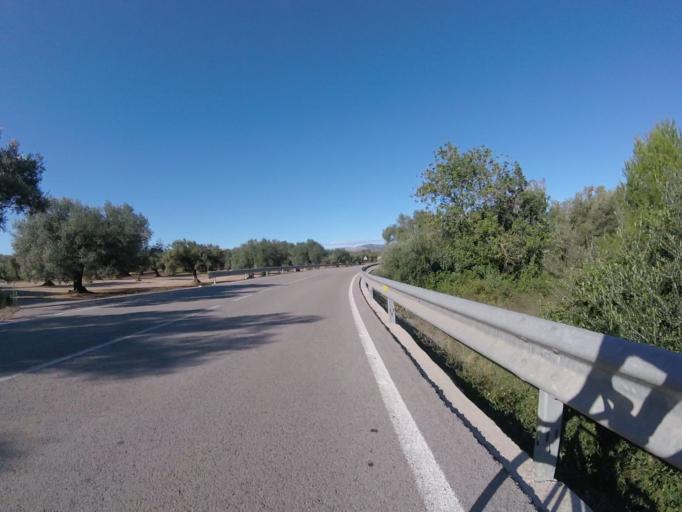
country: ES
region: Valencia
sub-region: Provincia de Castello
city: Cervera del Maestre
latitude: 40.4769
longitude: 0.2200
